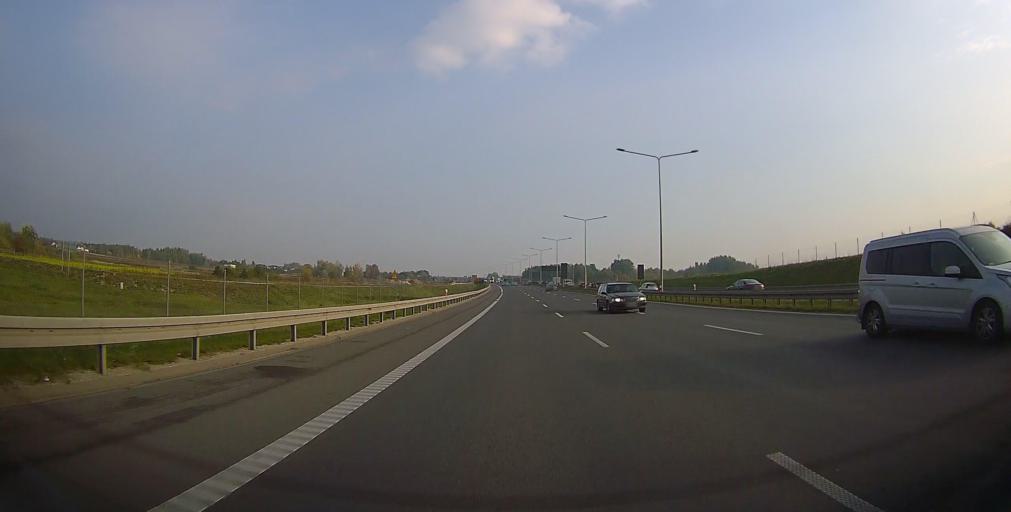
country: PL
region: Masovian Voivodeship
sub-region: Powiat pruszkowski
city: Nowe Grocholice
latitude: 52.1523
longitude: 20.8966
